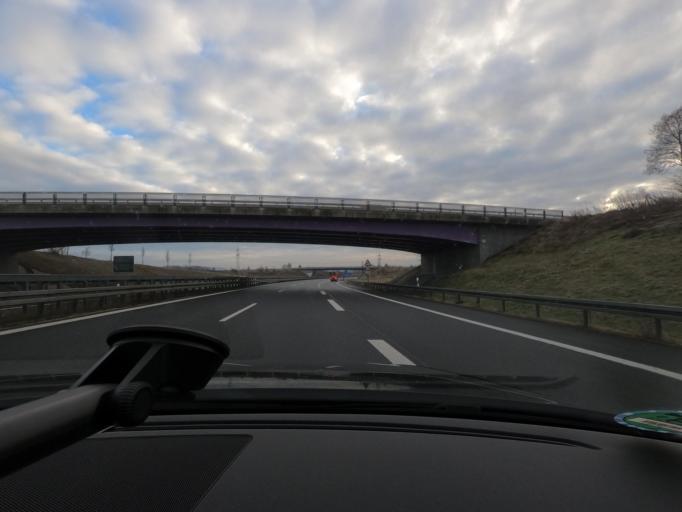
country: DE
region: Bavaria
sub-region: Upper Franconia
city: Rodental
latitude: 50.2957
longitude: 11.0021
